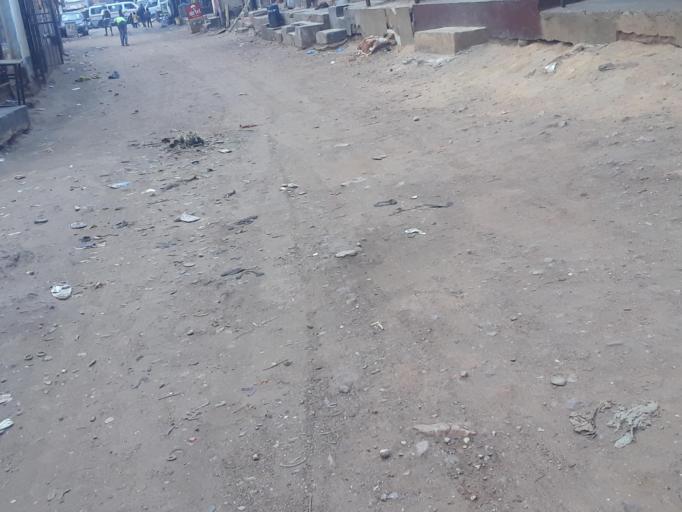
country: ZM
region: Lusaka
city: Lusaka
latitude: -15.3647
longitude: 28.2951
